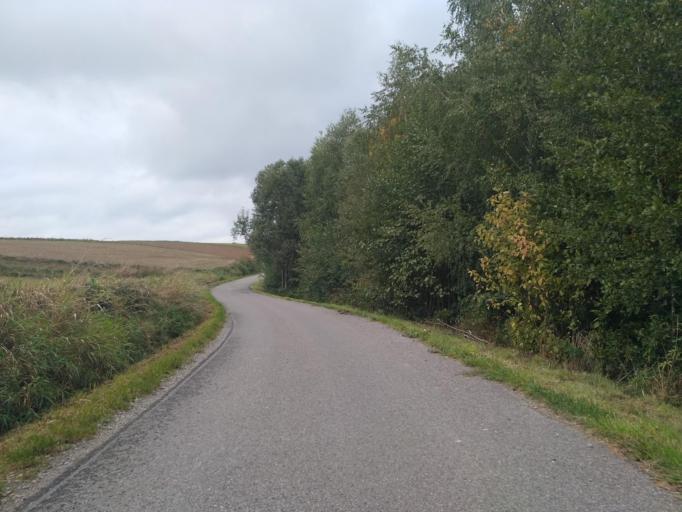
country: PL
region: Subcarpathian Voivodeship
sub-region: Powiat debicki
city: Brzostek
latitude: 49.9378
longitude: 21.4551
